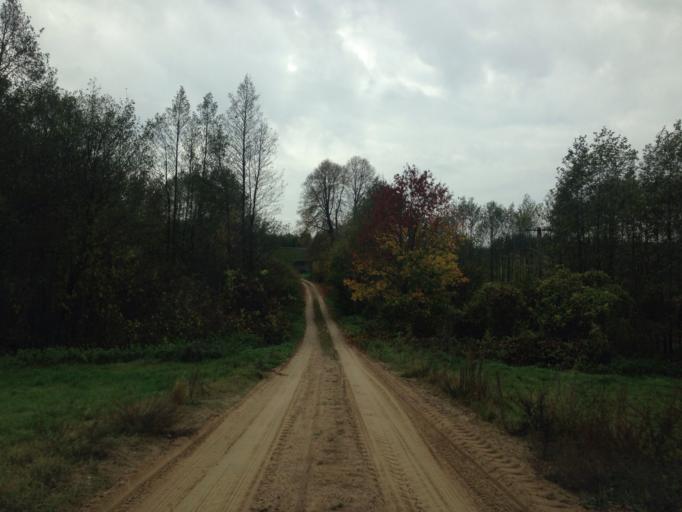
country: PL
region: Kujawsko-Pomorskie
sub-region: Powiat brodnicki
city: Bartniczka
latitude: 53.2697
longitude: 19.6721
